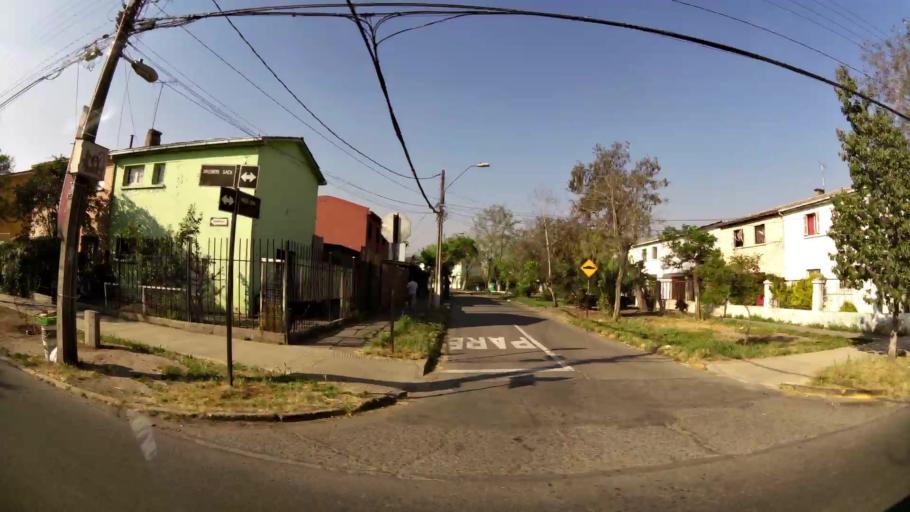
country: CL
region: Santiago Metropolitan
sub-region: Provincia de Santiago
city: Santiago
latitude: -33.4154
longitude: -70.6771
